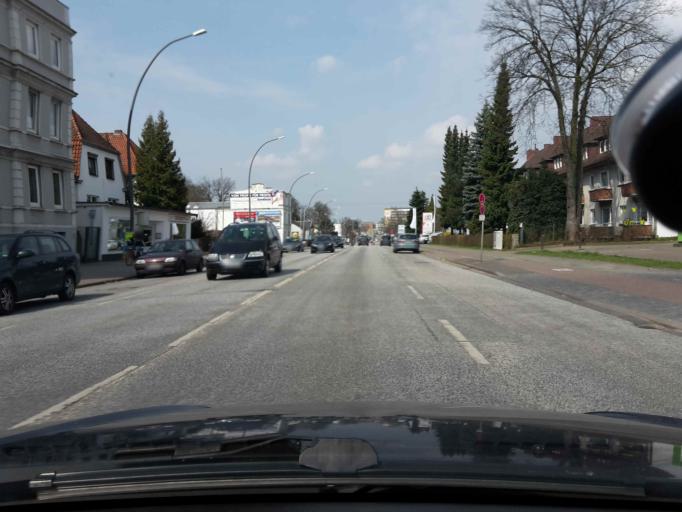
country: DE
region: Hamburg
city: Eidelstedt
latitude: 53.5860
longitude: 9.8787
